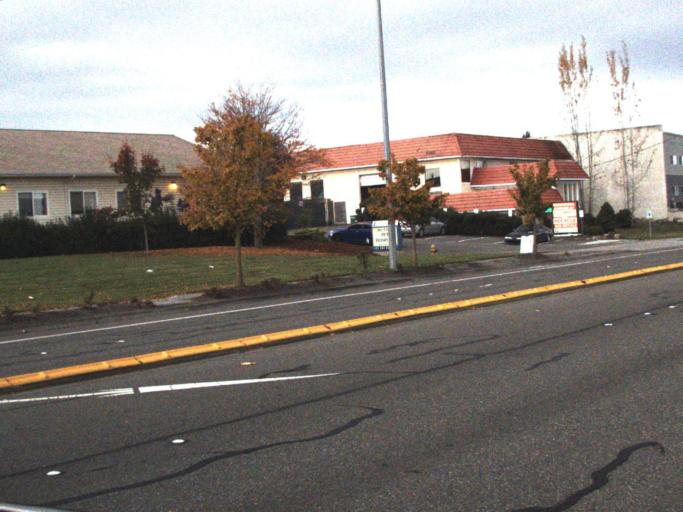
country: US
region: Washington
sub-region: Snohomish County
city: Mukilteo
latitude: 47.8968
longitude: -122.2896
